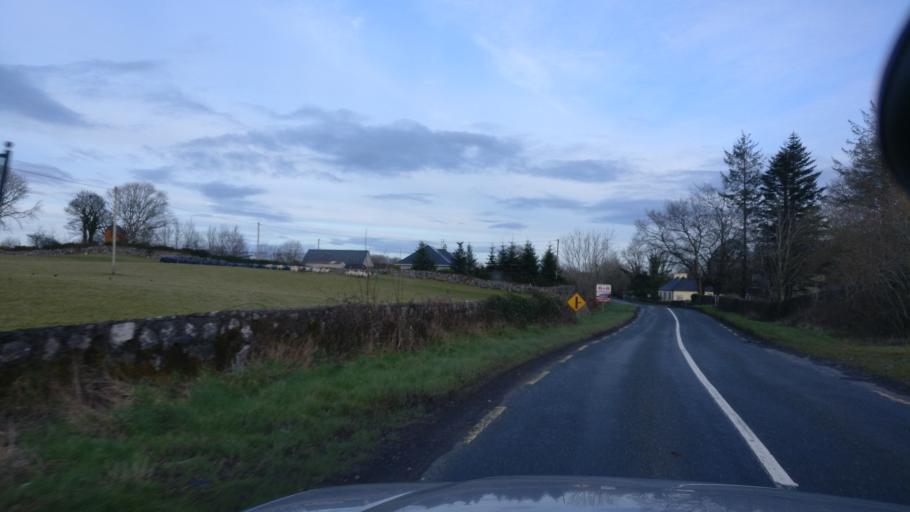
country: IE
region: Connaught
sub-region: Maigh Eo
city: Ballinrobe
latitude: 53.5399
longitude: -9.2435
